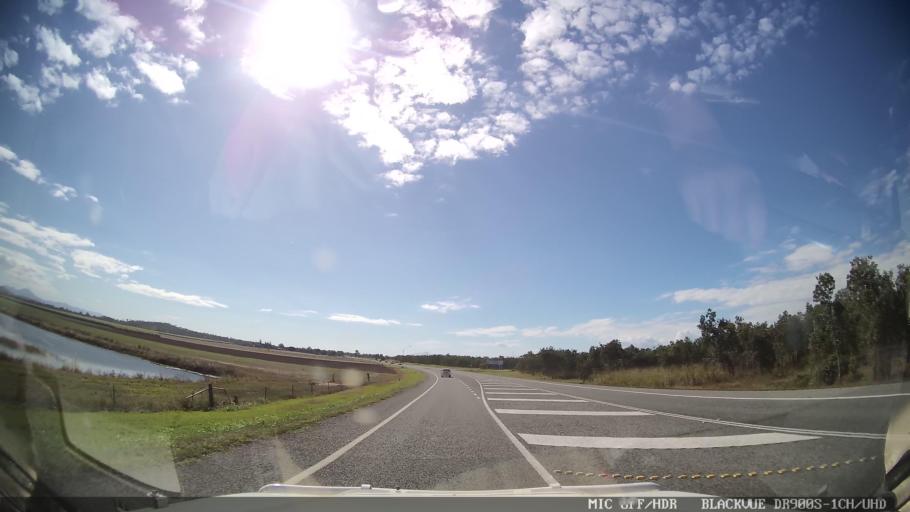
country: AU
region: Queensland
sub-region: Whitsunday
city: Proserpine
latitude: -20.5730
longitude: 148.6197
